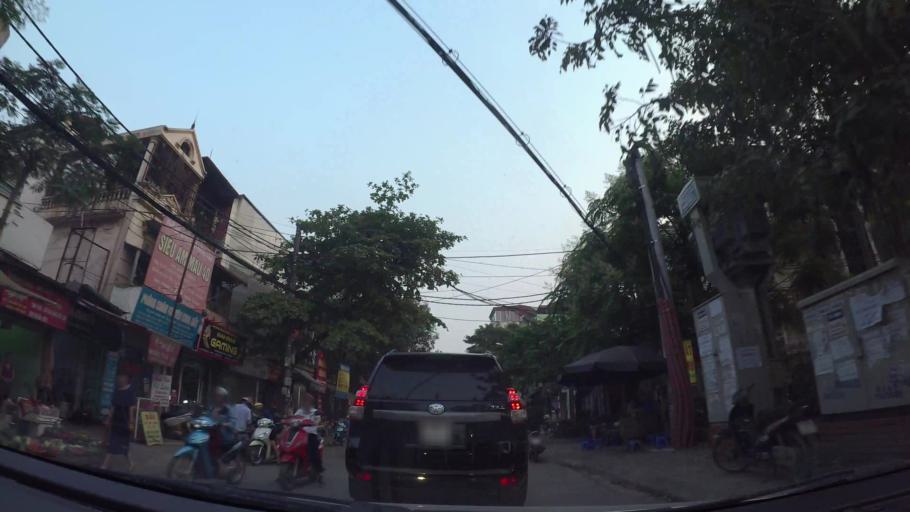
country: VN
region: Ha Noi
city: Cau Giay
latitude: 21.0483
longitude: 105.7900
